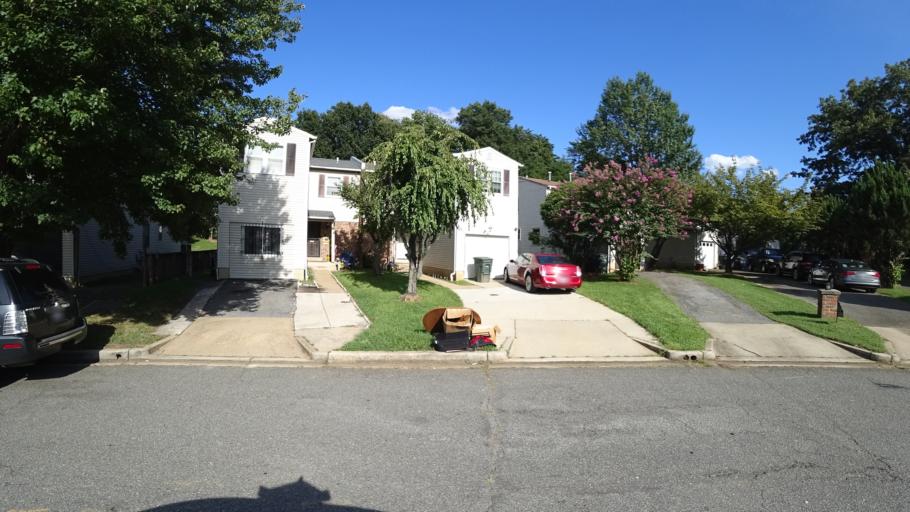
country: US
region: Maryland
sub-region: Prince George's County
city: Chillum
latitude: 38.9415
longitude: -76.9958
